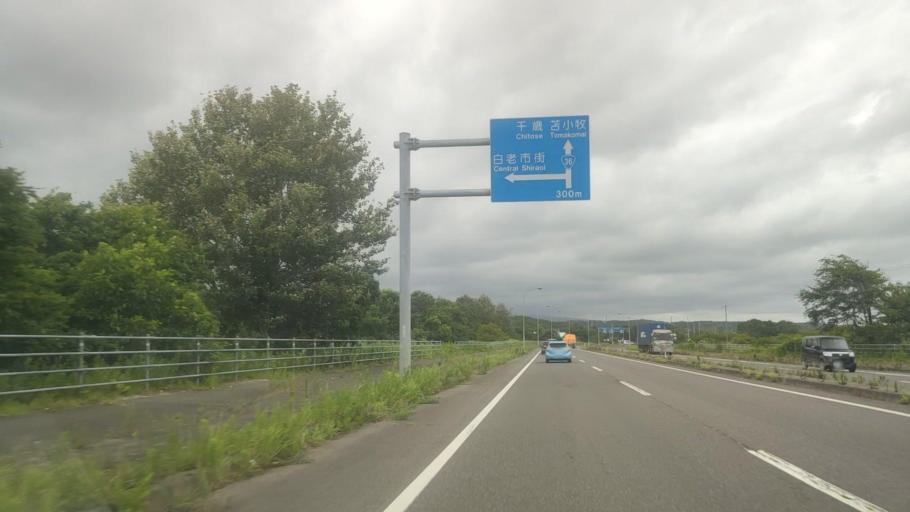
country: JP
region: Hokkaido
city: Shiraoi
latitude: 42.5609
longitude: 141.3807
